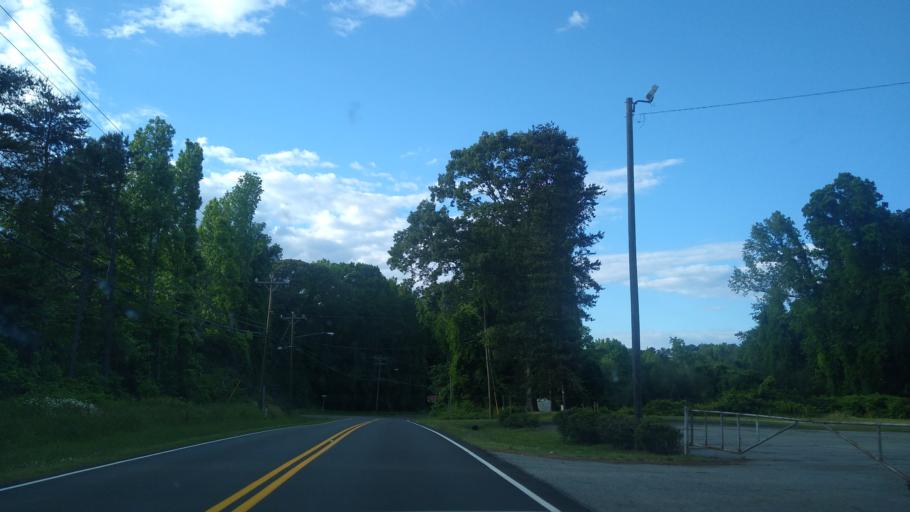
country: US
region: North Carolina
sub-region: Guilford County
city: McLeansville
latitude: 36.1583
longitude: -79.7362
